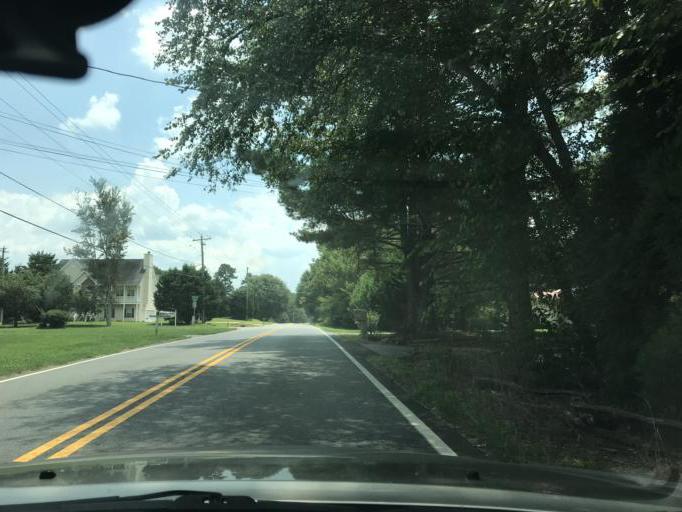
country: US
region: Georgia
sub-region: Forsyth County
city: Cumming
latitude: 34.2702
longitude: -84.2361
